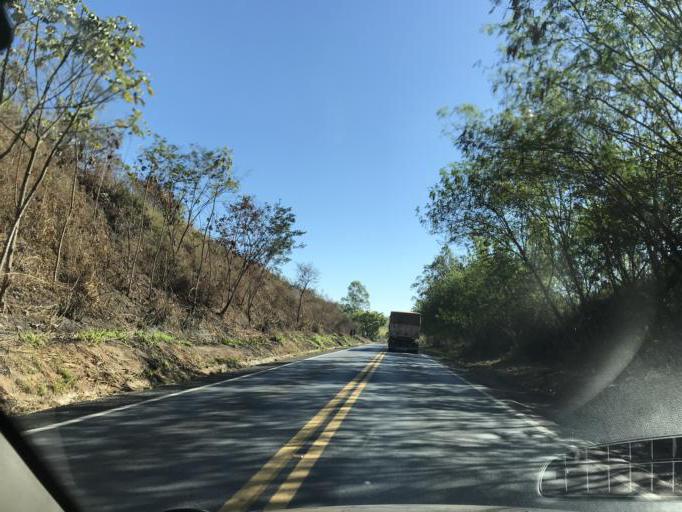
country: BR
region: Minas Gerais
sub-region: Bambui
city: Bambui
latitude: -19.8551
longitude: -45.9882
